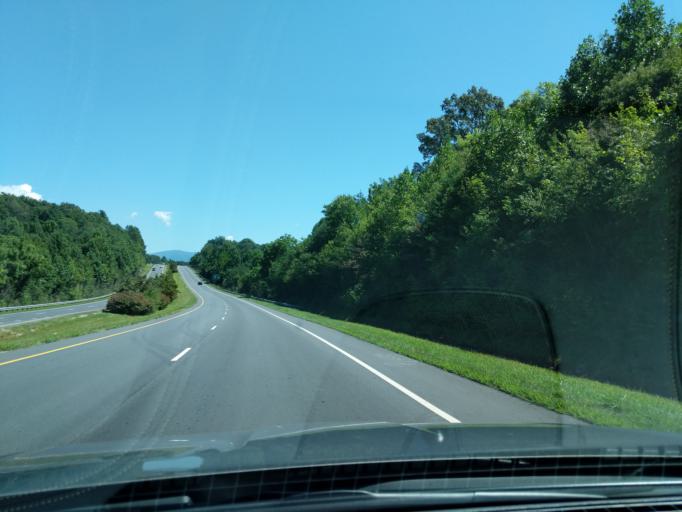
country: US
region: North Carolina
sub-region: Macon County
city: Franklin
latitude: 35.1641
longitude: -83.4157
